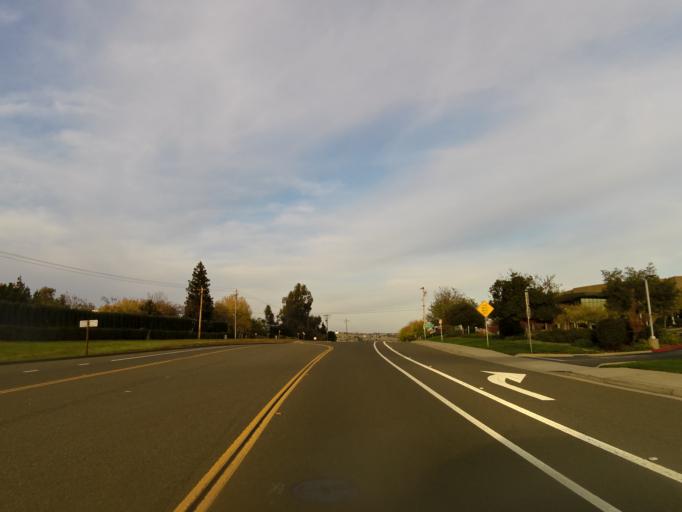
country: US
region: California
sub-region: El Dorado County
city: El Dorado Hills
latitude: 38.6403
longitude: -121.0750
